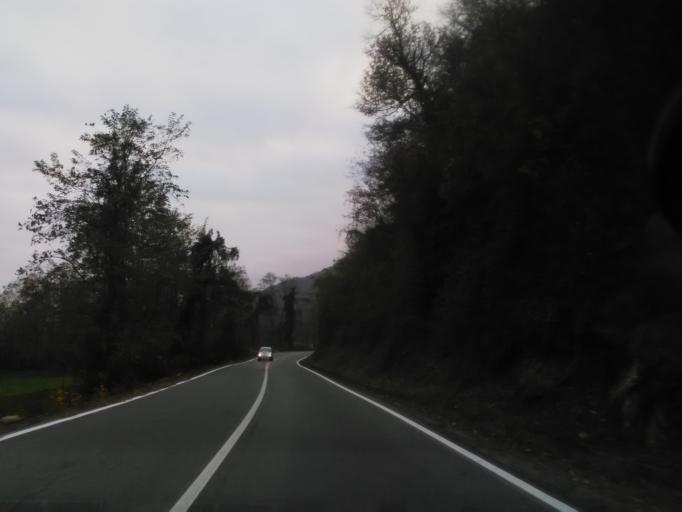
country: IT
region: Piedmont
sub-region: Provincia di Vercelli
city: Varallo
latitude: 45.7907
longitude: 8.2658
